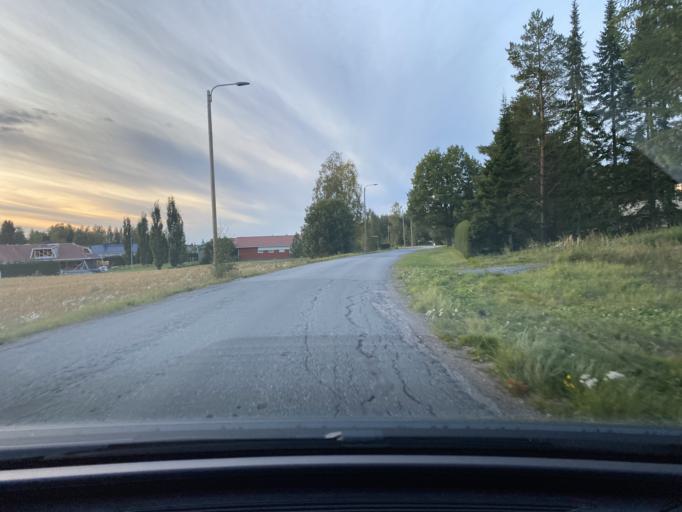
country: FI
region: Satakunta
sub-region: Pori
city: Huittinen
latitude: 61.1704
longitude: 22.7161
